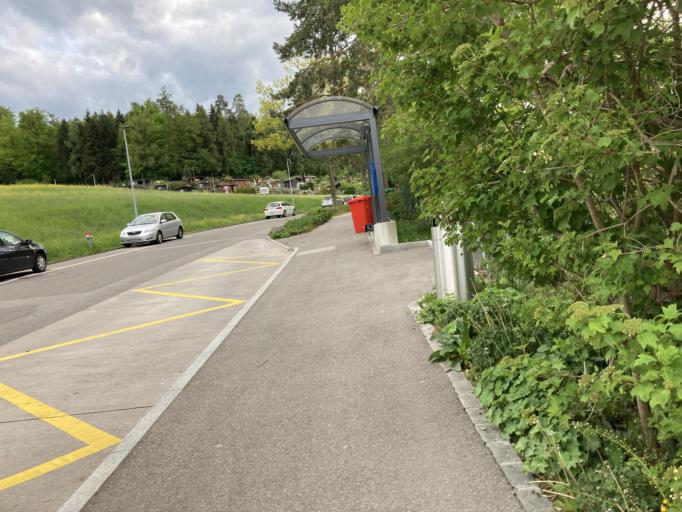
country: CH
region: Zurich
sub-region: Bezirk Horgen
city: Adliswil / Tal
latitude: 47.3084
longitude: 8.5341
